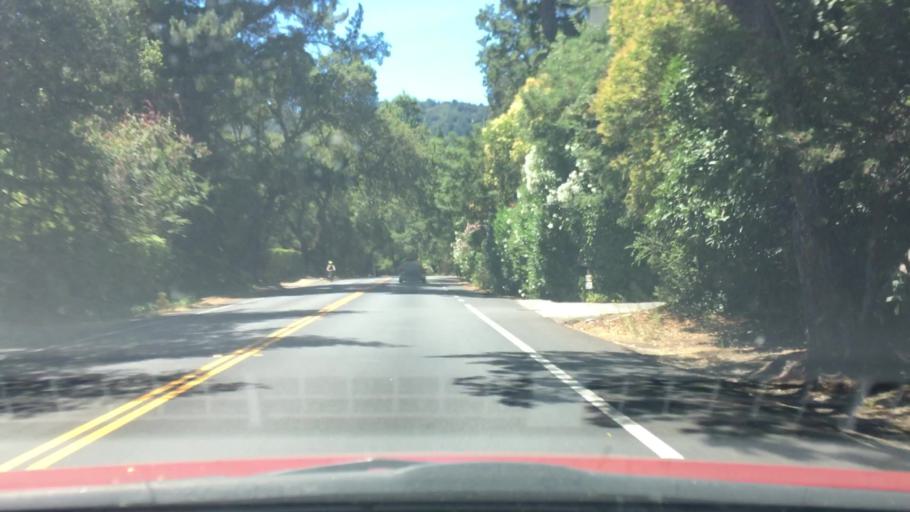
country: US
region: California
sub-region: San Mateo County
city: Woodside
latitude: 37.4266
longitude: -122.2646
